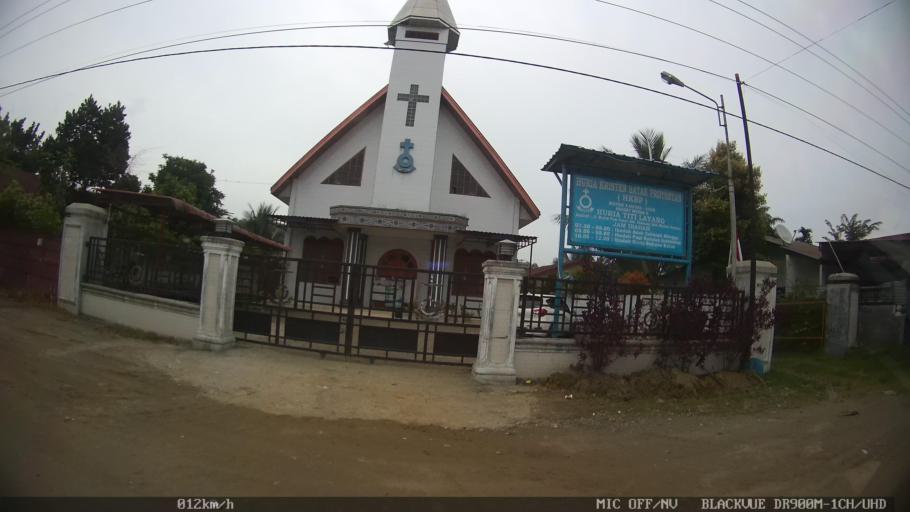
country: ID
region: North Sumatra
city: Deli Tua
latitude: 3.5402
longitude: 98.7351
